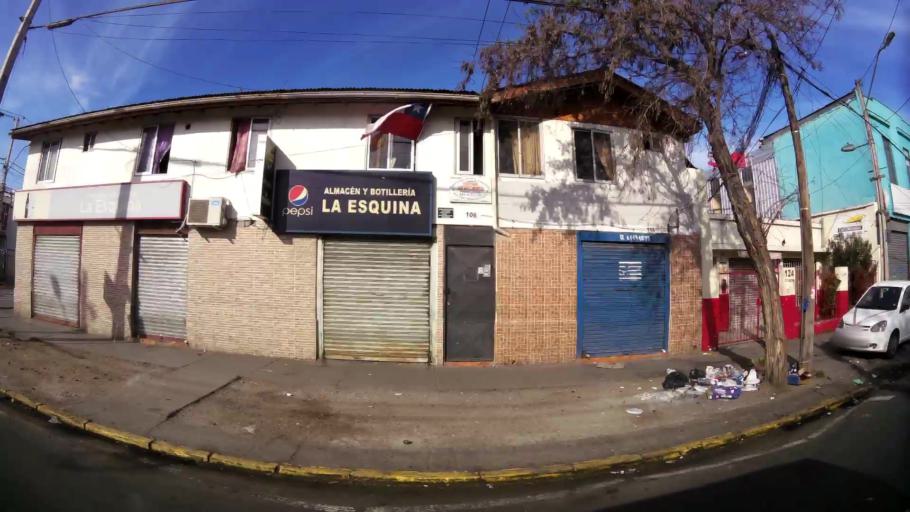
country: CL
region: Santiago Metropolitan
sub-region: Provincia de Santiago
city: Santiago
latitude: -33.4545
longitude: -70.6855
